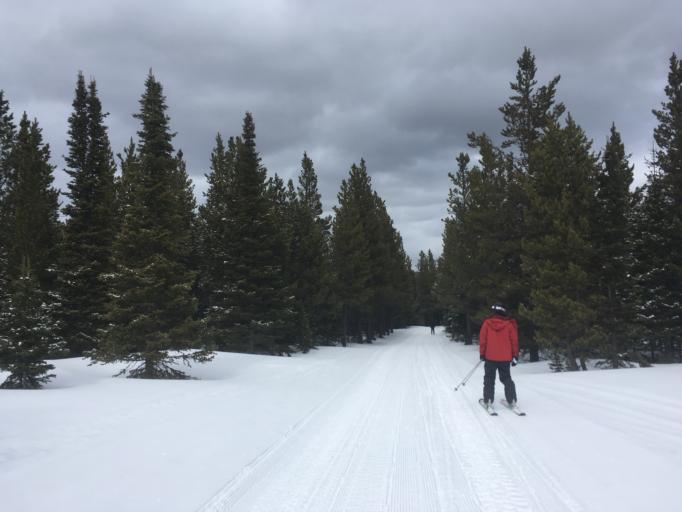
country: US
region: Montana
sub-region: Meagher County
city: White Sulphur Springs
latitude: 46.8469
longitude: -110.7036
